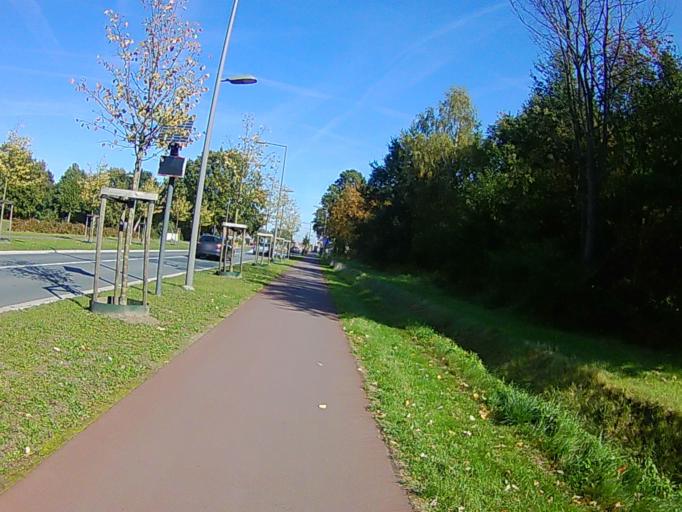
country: BE
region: Flanders
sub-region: Provincie Antwerpen
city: Stabroek
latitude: 51.3442
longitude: 4.3913
